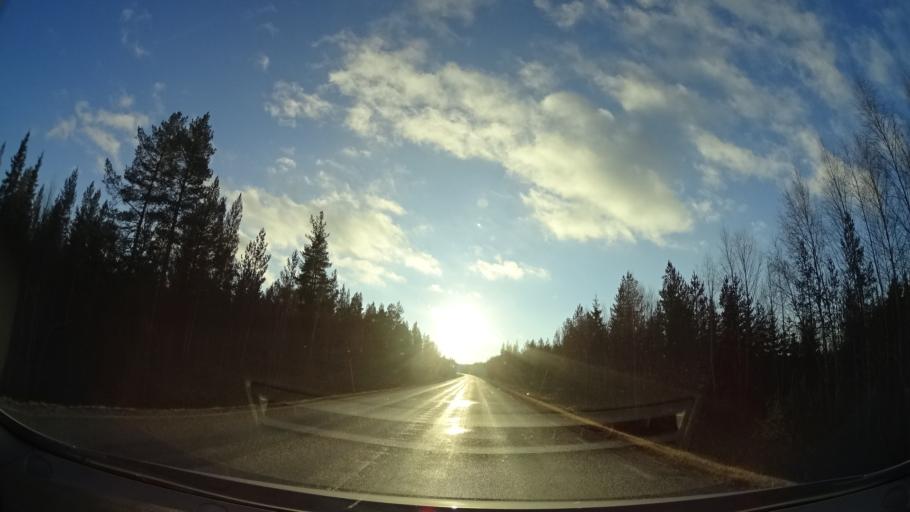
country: SE
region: Vaesterbotten
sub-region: Lycksele Kommun
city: Lycksele
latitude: 64.7721
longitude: 18.7249
